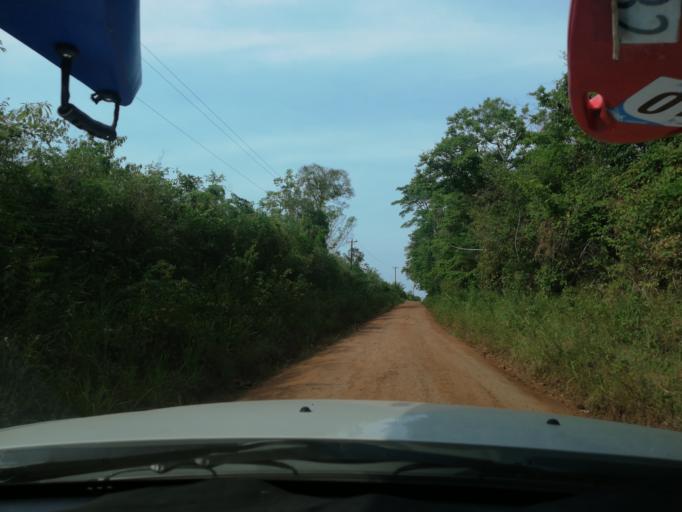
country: AR
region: Misiones
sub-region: Departamento de San Ignacio
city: San Ignacio
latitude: -27.2949
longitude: -55.5694
